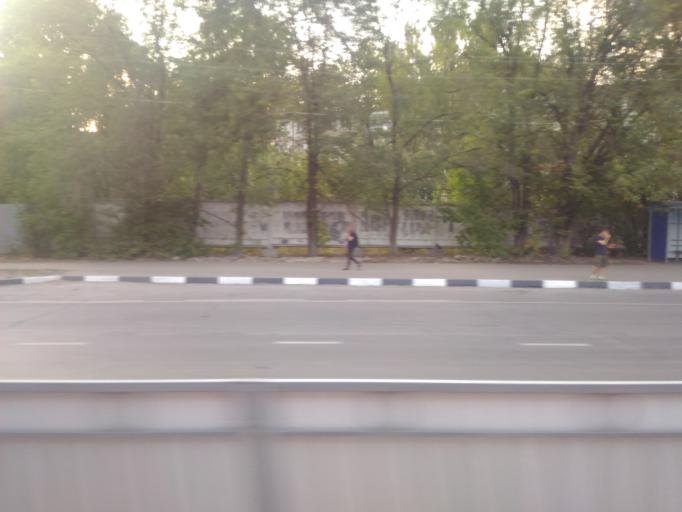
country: RU
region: Ulyanovsk
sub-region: Ulyanovskiy Rayon
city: Ulyanovsk
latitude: 54.2883
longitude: 48.3042
